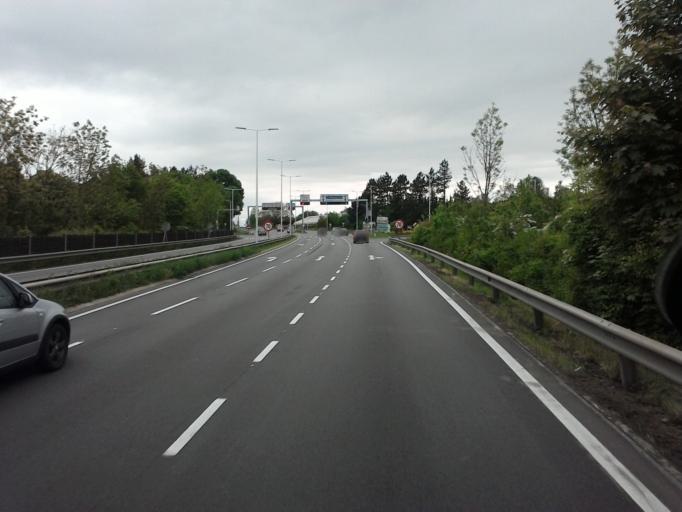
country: AT
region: Upper Austria
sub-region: Wels-Land
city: Thalheim bei Wels
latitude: 48.1523
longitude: 14.0440
